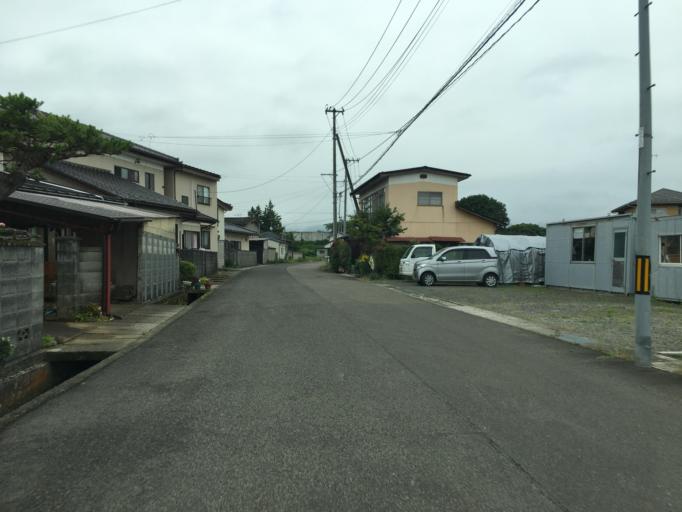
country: JP
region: Fukushima
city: Fukushima-shi
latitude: 37.7542
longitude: 140.4114
